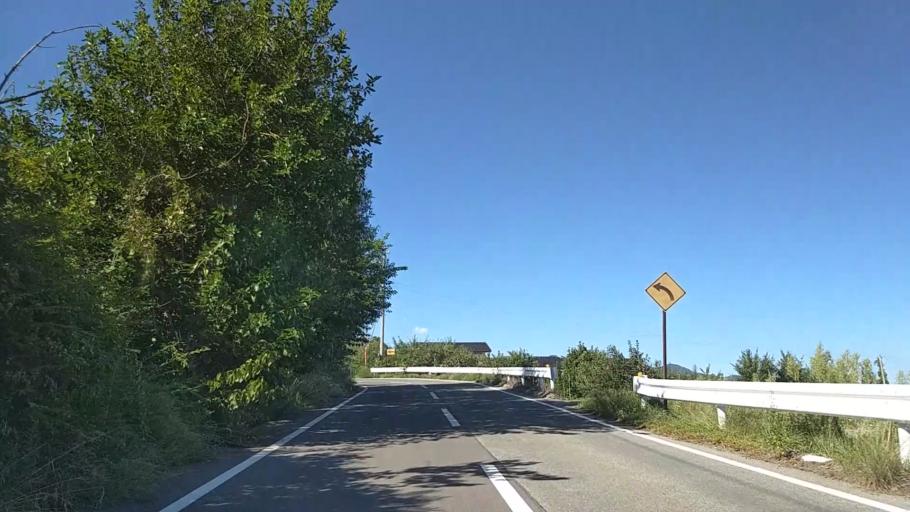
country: JP
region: Nagano
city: Nagano-shi
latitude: 36.5834
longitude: 138.1243
